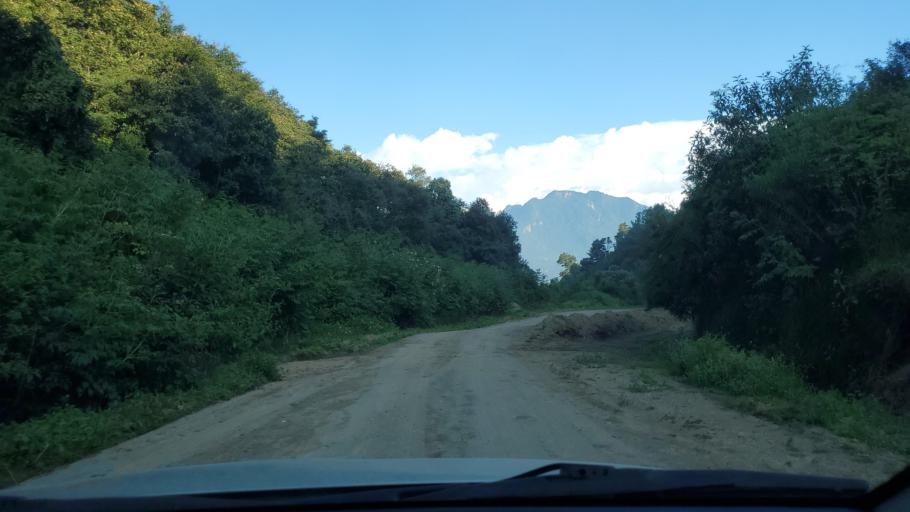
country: GT
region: Quetzaltenango
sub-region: Municipio de La Esperanza
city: La Esperanza
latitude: 14.8390
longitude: -91.5539
